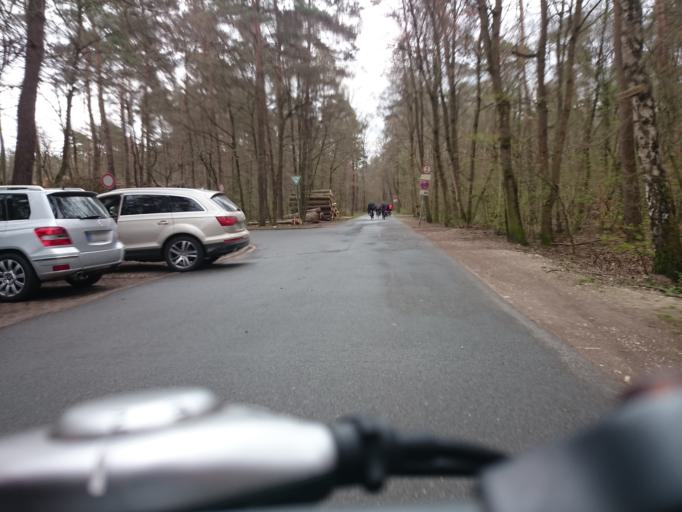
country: DE
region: Bavaria
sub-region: Regierungsbezirk Mittelfranken
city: Nuernberg
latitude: 49.4460
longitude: 11.1391
